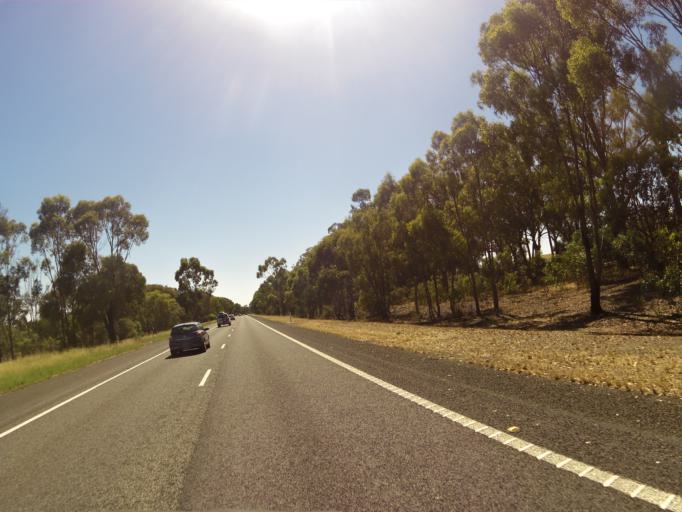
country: AU
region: Victoria
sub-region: Greater Shepparton
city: Shepparton
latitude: -36.8663
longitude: 145.2955
